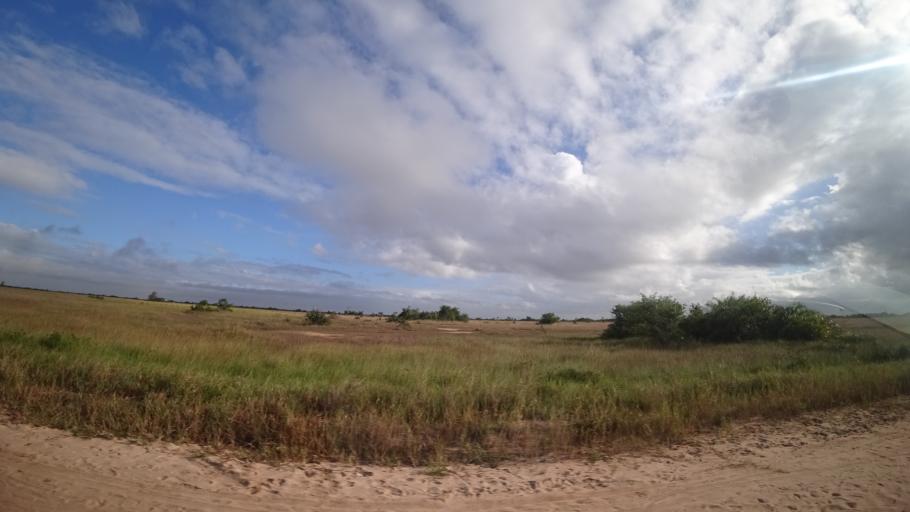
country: MZ
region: Sofala
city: Beira
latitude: -19.6841
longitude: 35.0520
